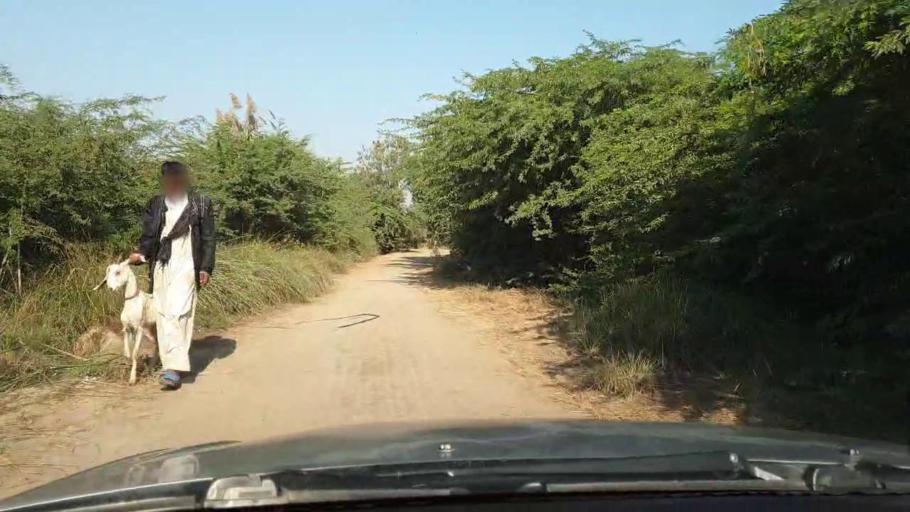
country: PK
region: Sindh
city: Matli
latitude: 25.0281
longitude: 68.5736
